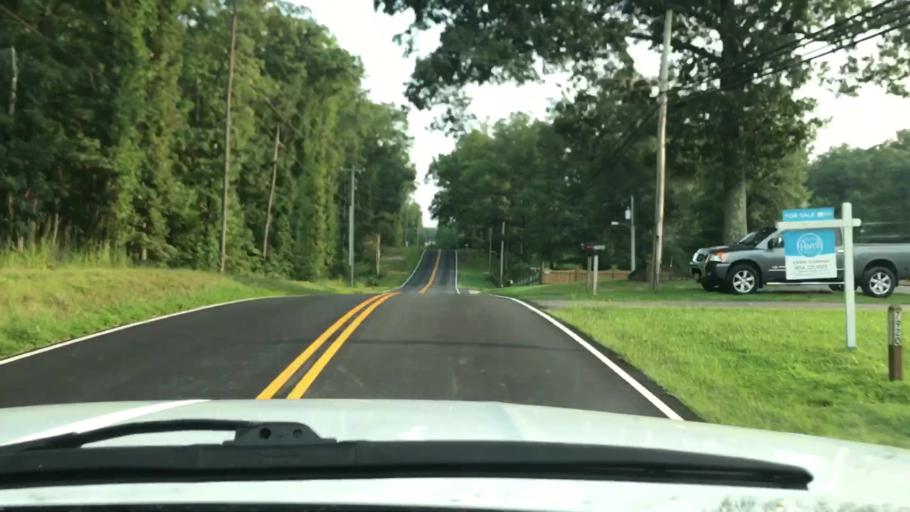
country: US
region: Virginia
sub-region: Chesterfield County
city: Chesterfield
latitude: 37.4237
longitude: -77.5345
